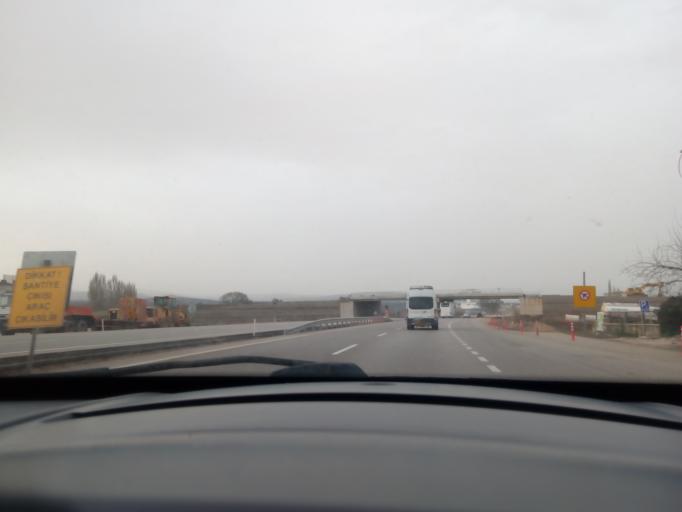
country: TR
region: Bursa
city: Tatkavakli
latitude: 40.0346
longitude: 28.3738
